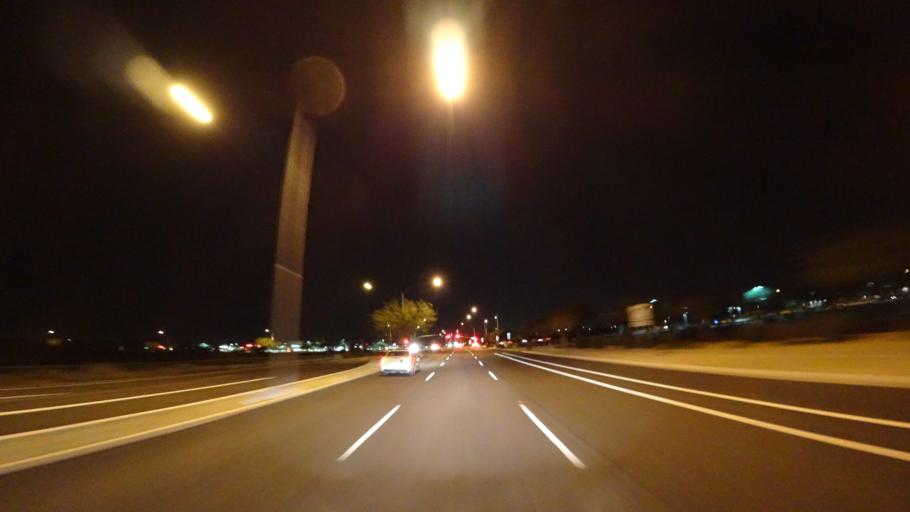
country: US
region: Arizona
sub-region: Pinal County
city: Apache Junction
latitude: 33.3791
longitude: -111.6168
